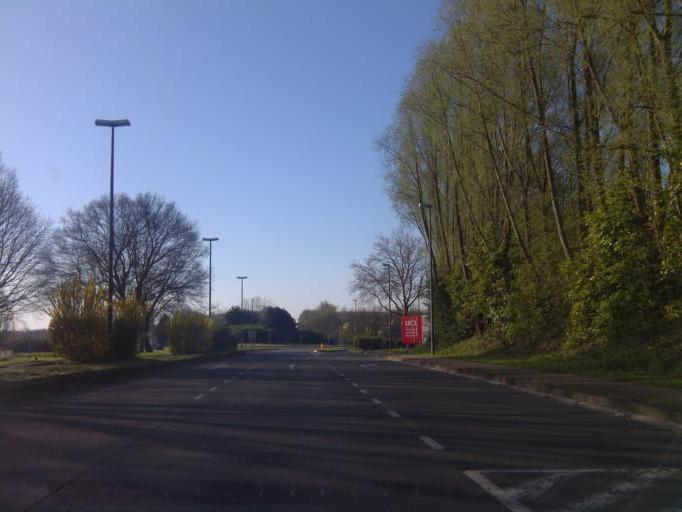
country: BE
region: Wallonia
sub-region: Province du Brabant Wallon
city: Louvain-la-Neuve
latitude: 50.6777
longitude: 4.6223
